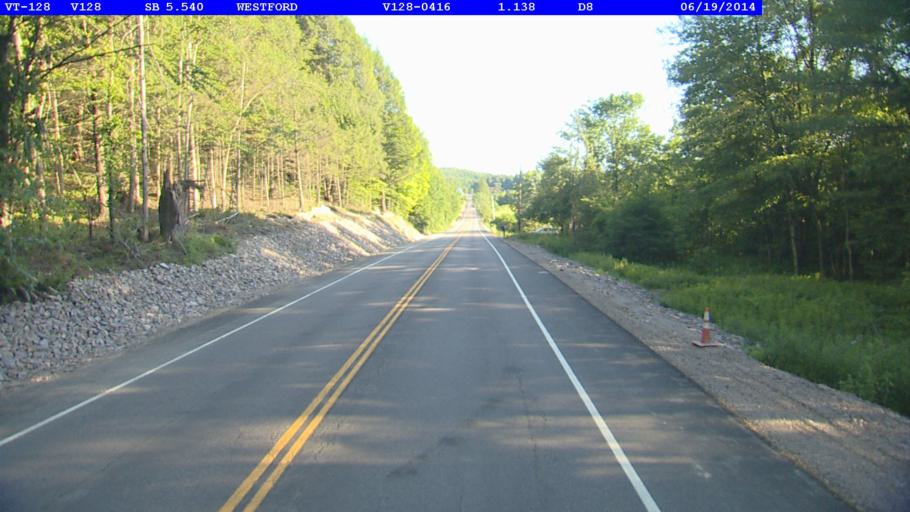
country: US
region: Vermont
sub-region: Chittenden County
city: Jericho
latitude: 44.5745
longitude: -73.0204
